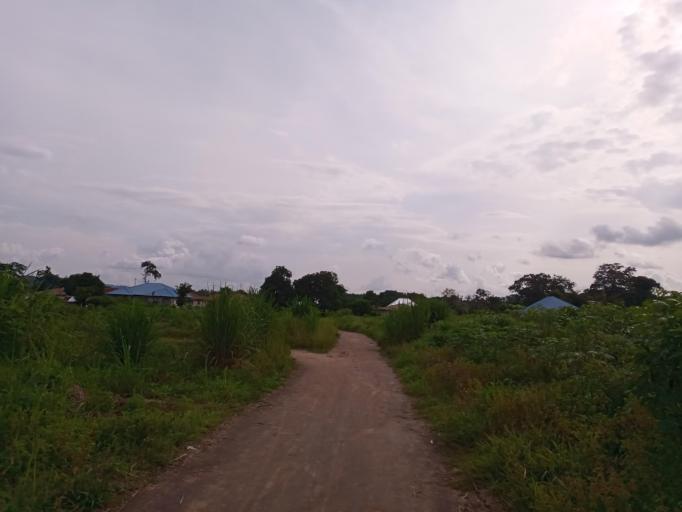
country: SL
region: Northern Province
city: Bumbuna
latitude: 9.0493
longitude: -11.7548
